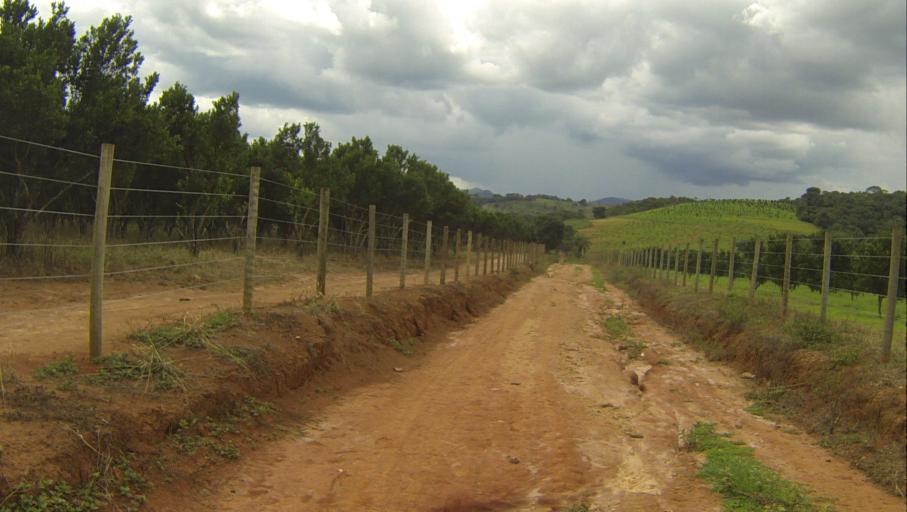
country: BR
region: Minas Gerais
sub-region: Brumadinho
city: Brumadinho
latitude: -20.1534
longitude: -44.1237
